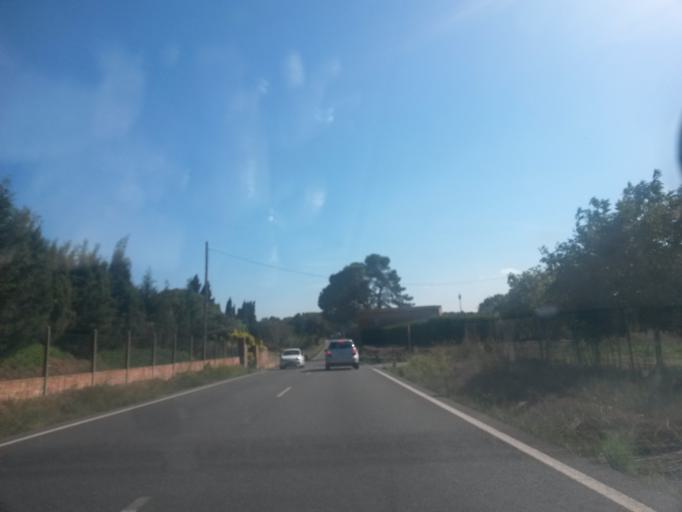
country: ES
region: Catalonia
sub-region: Provincia de Girona
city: Regencos
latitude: 41.9474
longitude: 3.1653
